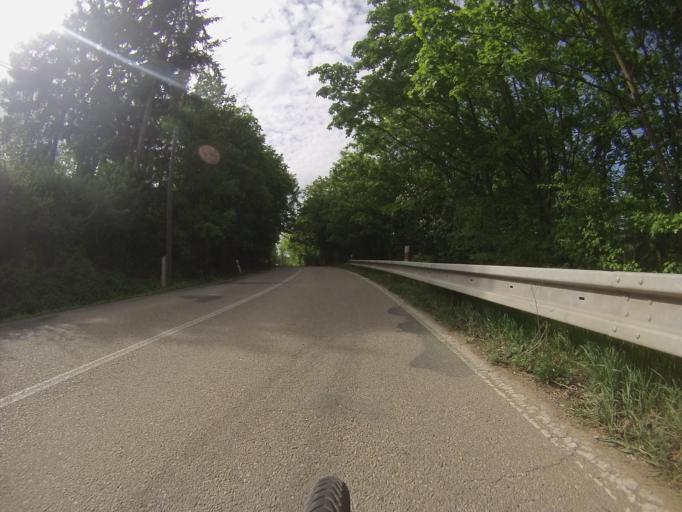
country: CZ
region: South Moravian
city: Kurim
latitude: 49.2391
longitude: 16.5044
